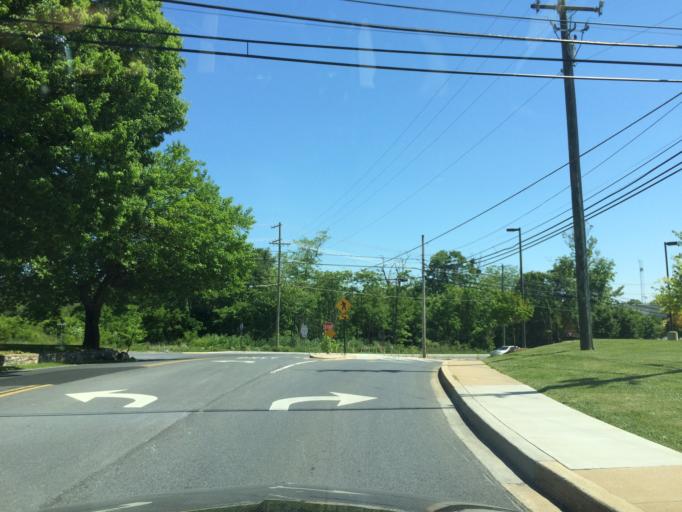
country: US
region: Maryland
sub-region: Frederick County
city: Frederick
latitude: 39.4442
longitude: -77.3951
